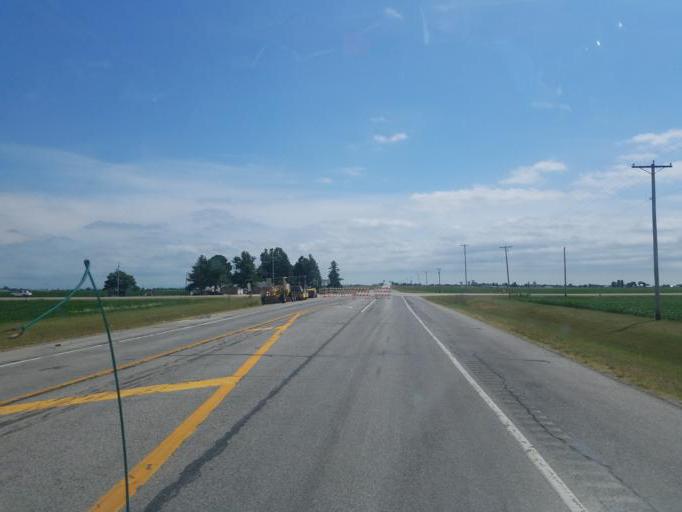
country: US
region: Indiana
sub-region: Allen County
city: Woodburn
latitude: 41.1554
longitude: -84.8488
